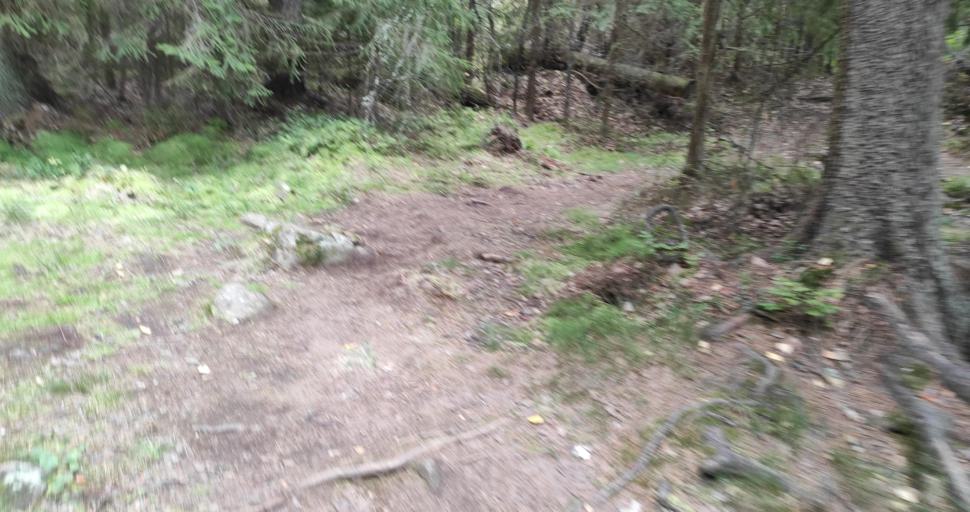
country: RU
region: Leningrad
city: Kuznechnoye
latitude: 61.1740
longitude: 29.6958
